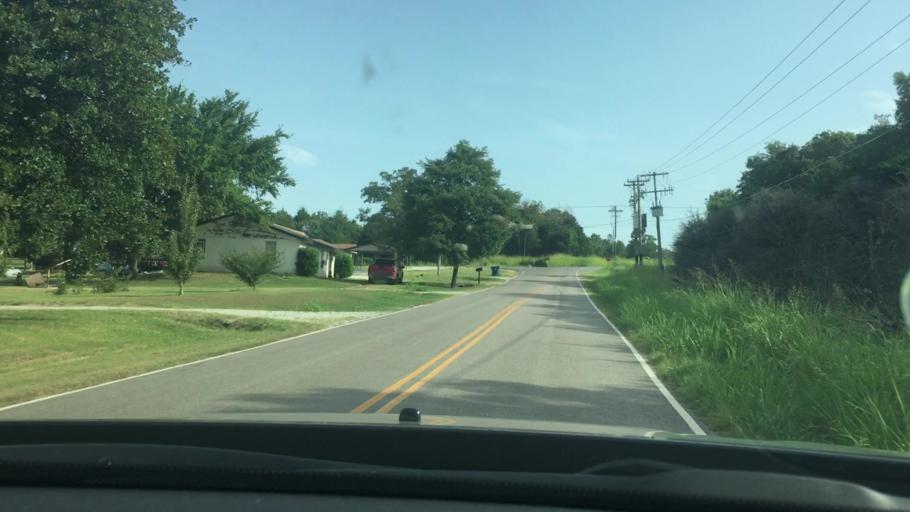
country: US
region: Oklahoma
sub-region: Pontotoc County
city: Byng
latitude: 34.8635
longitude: -96.6135
